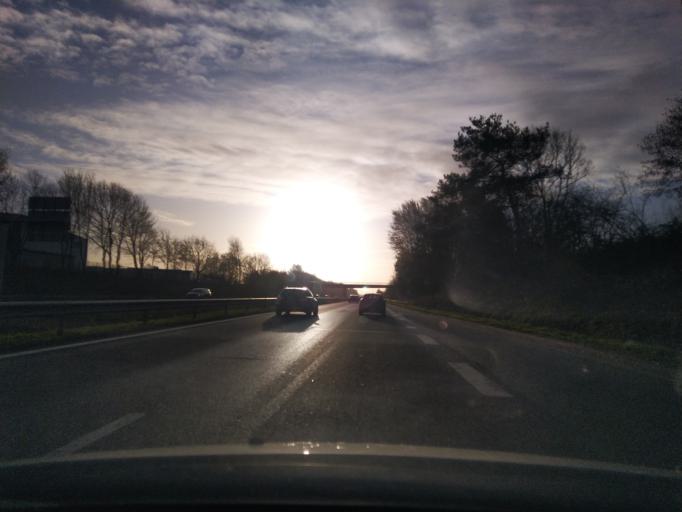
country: FR
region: Haute-Normandie
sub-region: Departement de la Seine-Maritime
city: Maromme
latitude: 49.4797
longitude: 1.0129
